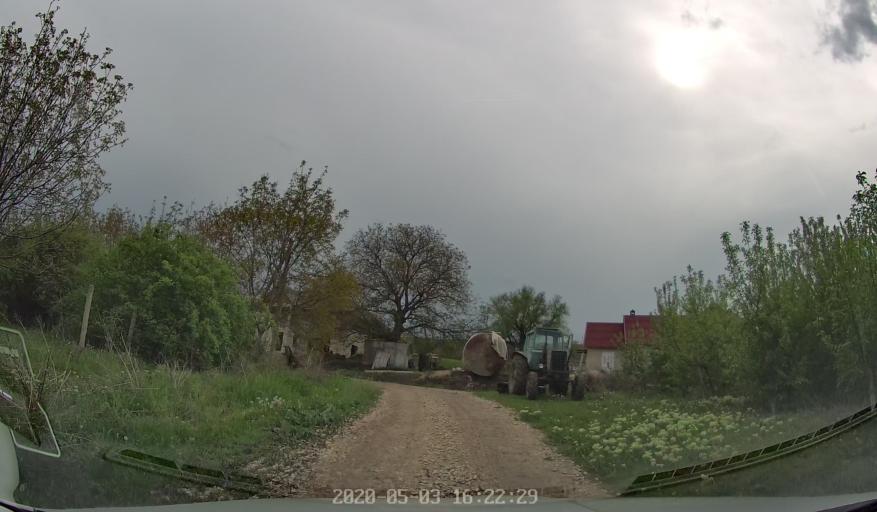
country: MD
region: Calarasi
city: Calarasi
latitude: 47.1993
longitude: 28.3475
